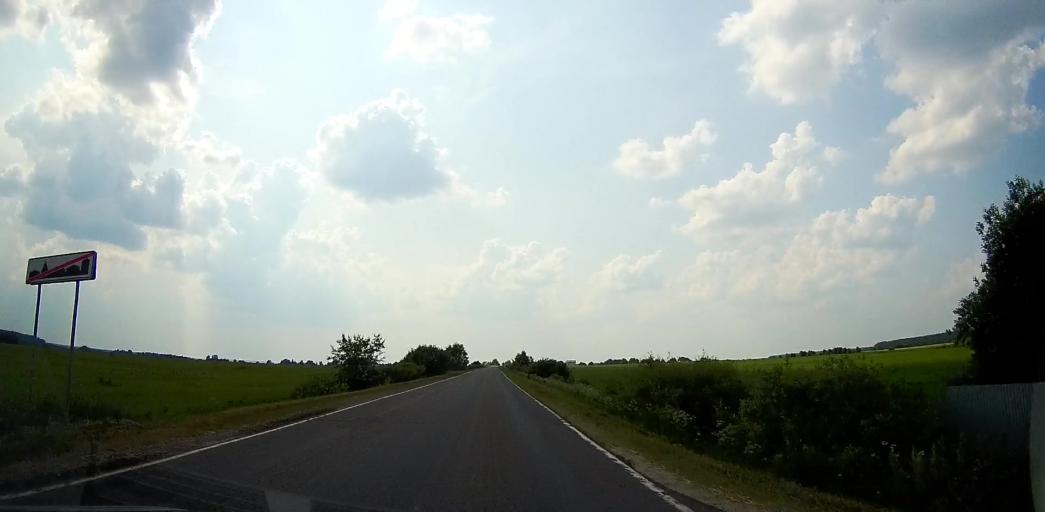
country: RU
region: Moskovskaya
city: Malino
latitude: 55.0644
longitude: 38.1186
